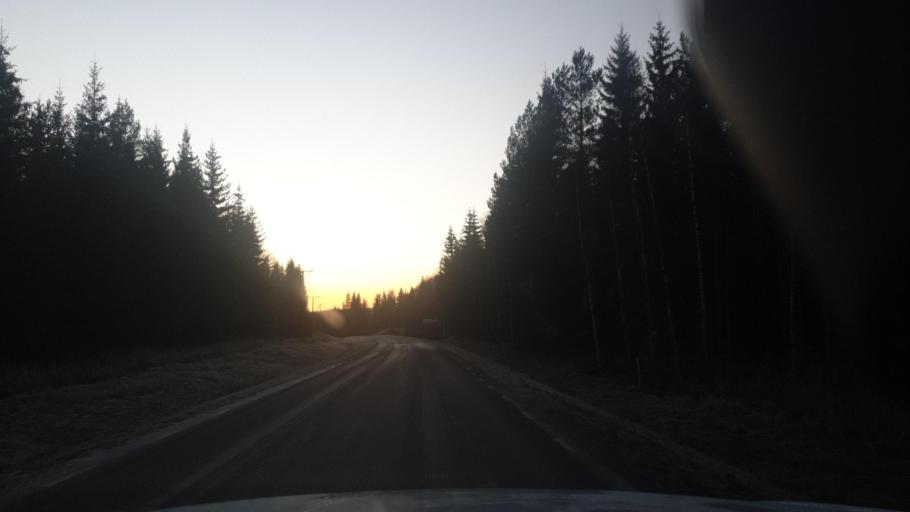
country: SE
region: Vaermland
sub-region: Eda Kommun
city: Charlottenberg
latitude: 59.9373
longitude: 12.3721
